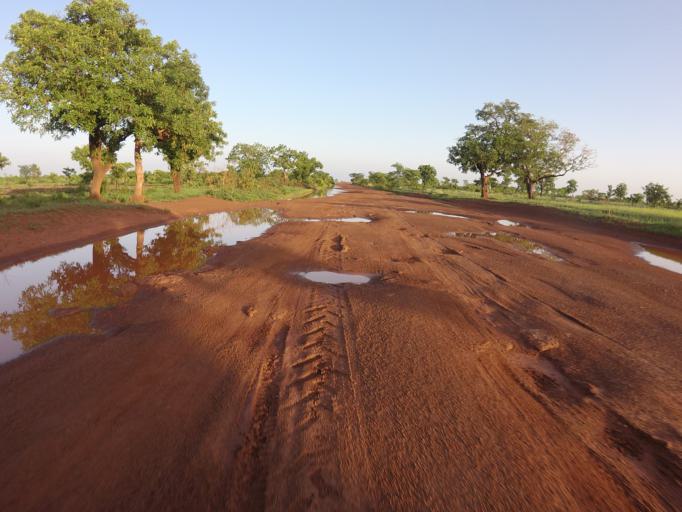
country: TG
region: Savanes
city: Sansanne-Mango
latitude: 10.2358
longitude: -0.0742
